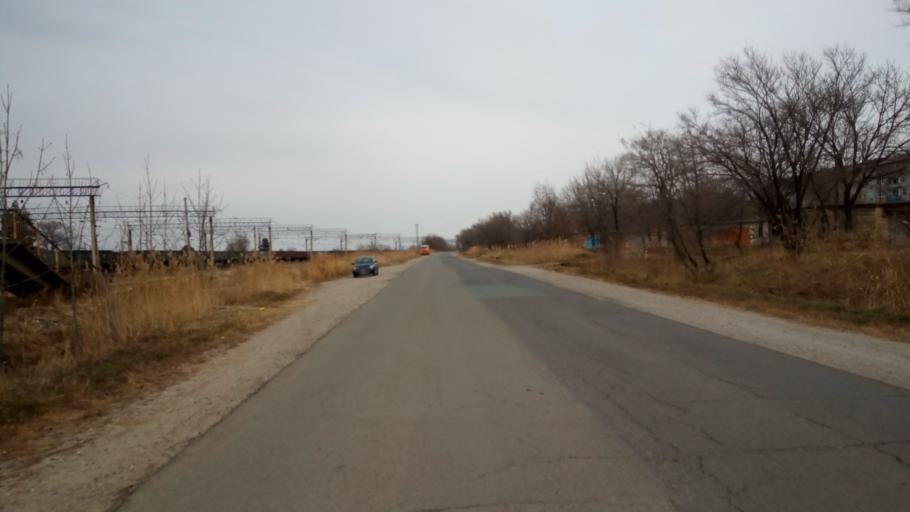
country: RU
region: Primorskiy
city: Novoshakhtinskiy
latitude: 44.0289
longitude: 132.1656
